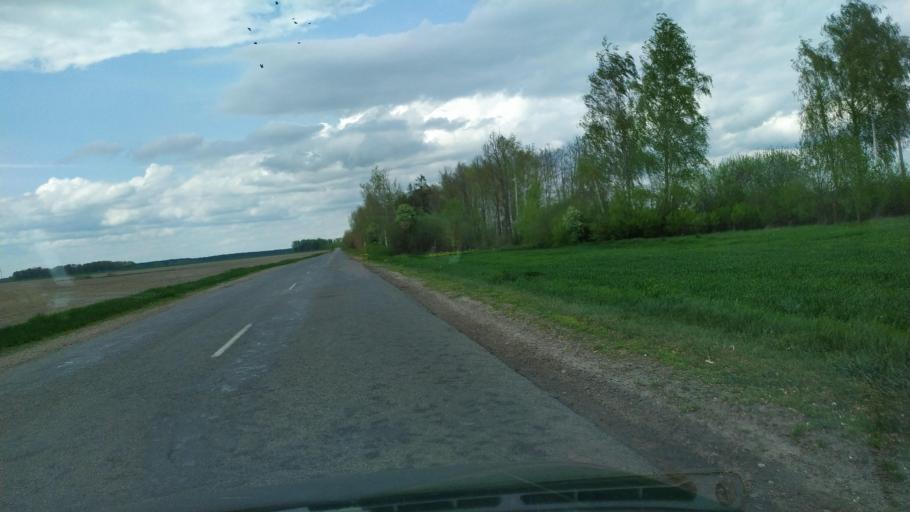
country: BY
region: Brest
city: Pruzhany
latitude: 52.6583
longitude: 24.3816
